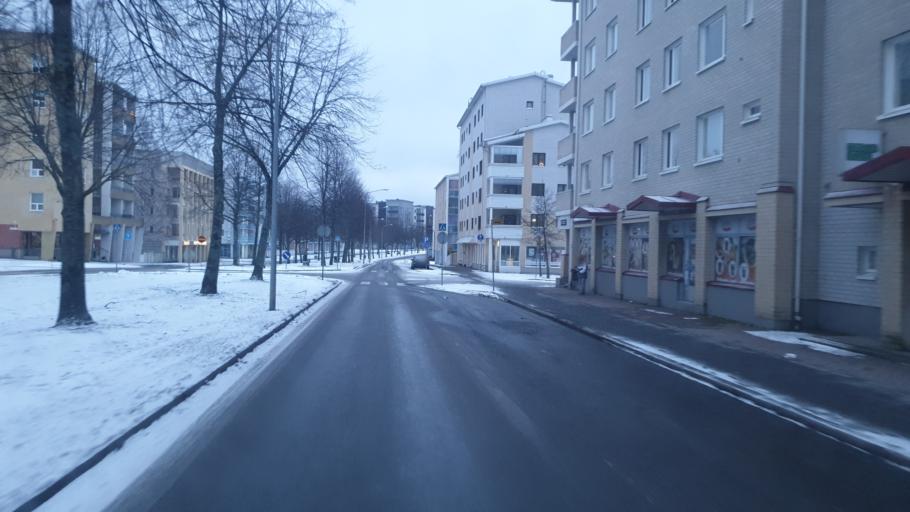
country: FI
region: Northern Savo
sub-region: Kuopio
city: Kuopio
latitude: 62.8389
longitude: 27.6389
